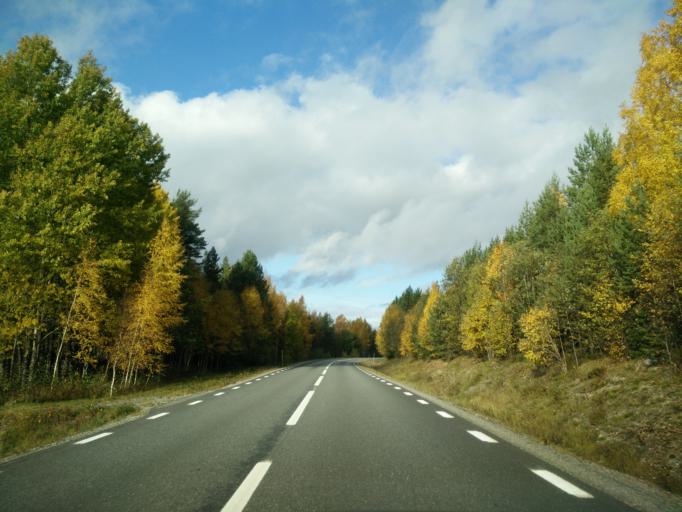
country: SE
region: Jaemtland
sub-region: Braecke Kommun
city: Braecke
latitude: 62.4029
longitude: 15.0211
